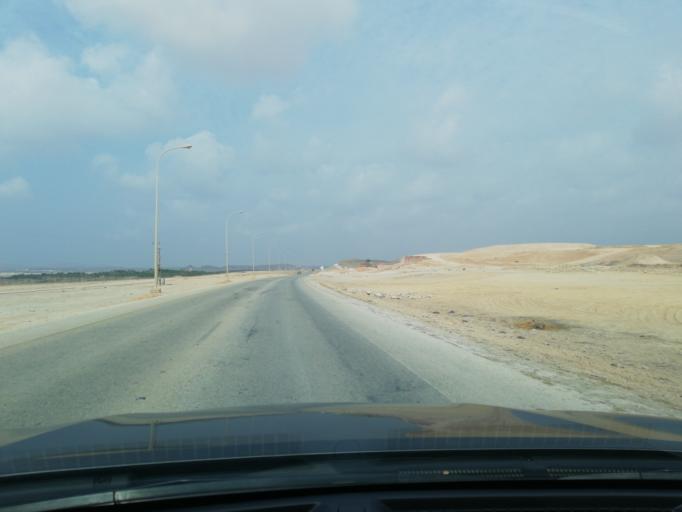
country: OM
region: Zufar
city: Salalah
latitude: 16.9468
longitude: 53.9587
